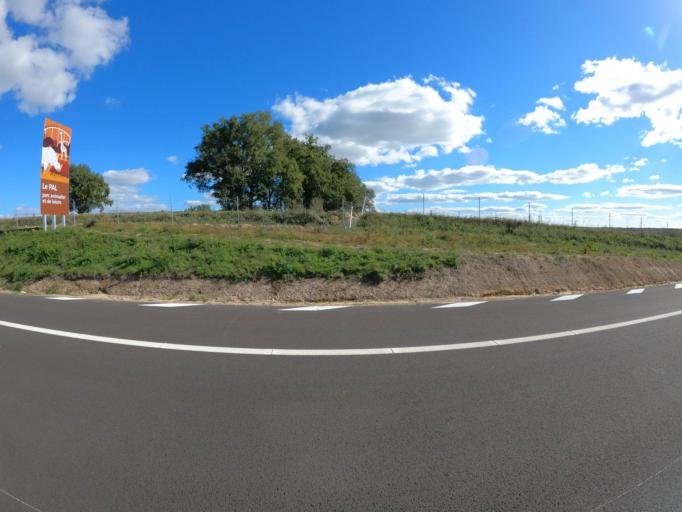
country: FR
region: Auvergne
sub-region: Departement de l'Allier
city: Lusigny
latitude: 46.5220
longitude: 3.4871
